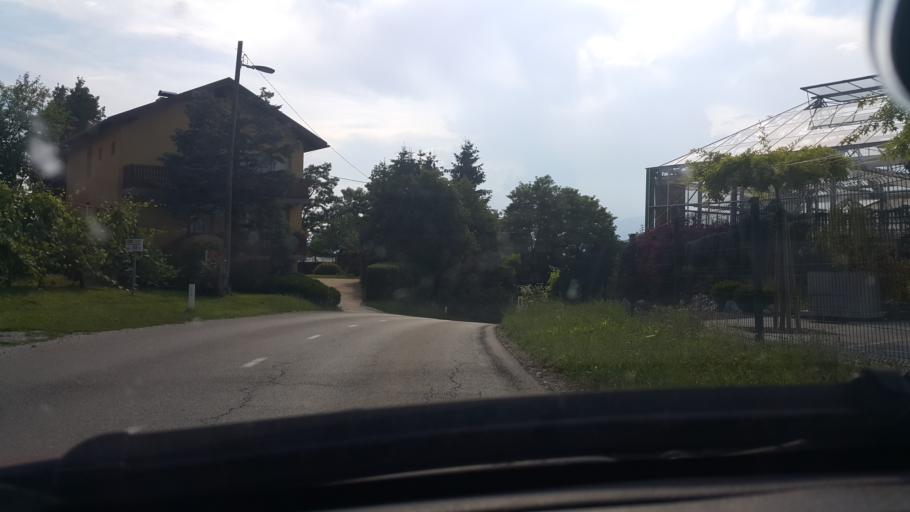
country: SI
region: Duplek
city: Spodnji Duplek
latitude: 46.4982
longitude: 15.7628
